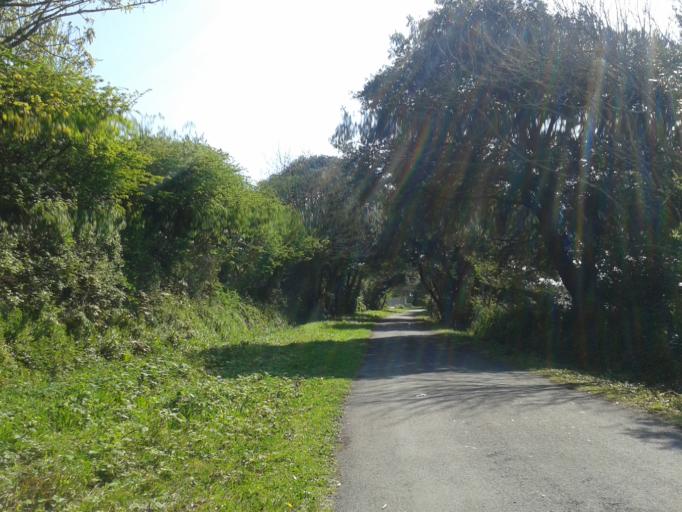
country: GB
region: England
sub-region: Devon
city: Fremington
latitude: 51.0941
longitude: -4.1087
